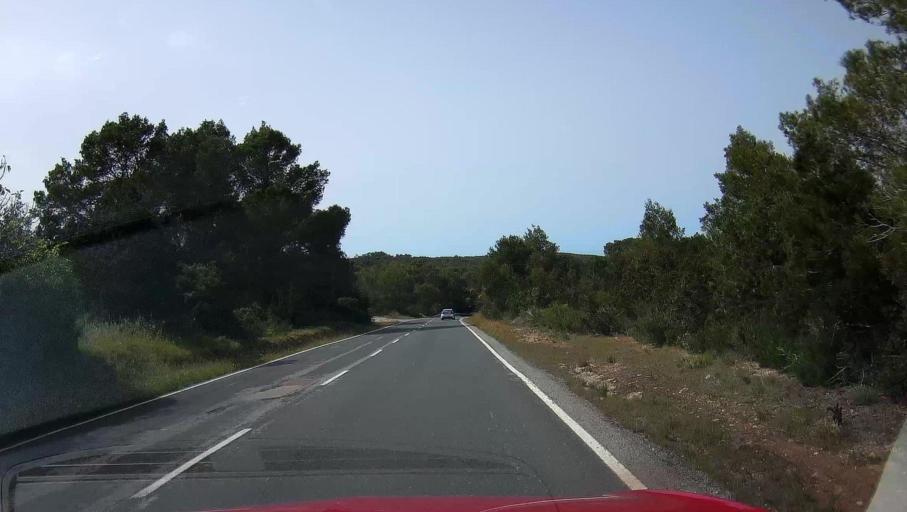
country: ES
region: Balearic Islands
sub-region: Illes Balears
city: Sant Joan de Labritja
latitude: 39.0932
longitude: 1.4999
